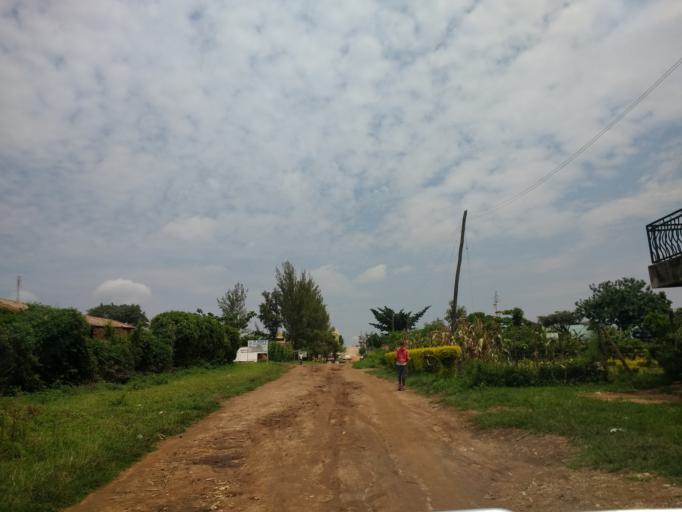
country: UG
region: Eastern Region
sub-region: Mbale District
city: Mbale
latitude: 1.0766
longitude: 34.1830
